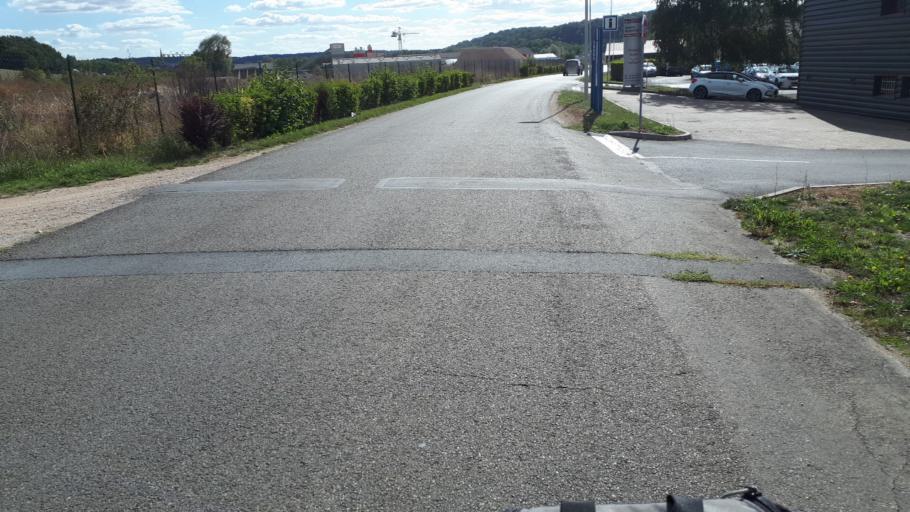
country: FR
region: Centre
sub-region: Departement du Loir-et-Cher
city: Villiers-sur-Loir
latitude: 47.7995
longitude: 0.9660
